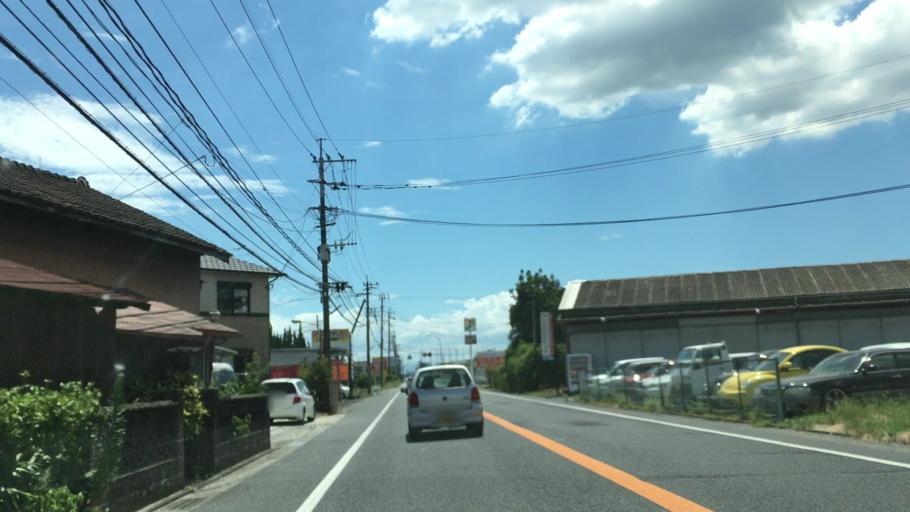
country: JP
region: Saga Prefecture
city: Kanzakimachi-kanzaki
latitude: 33.2830
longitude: 130.3457
